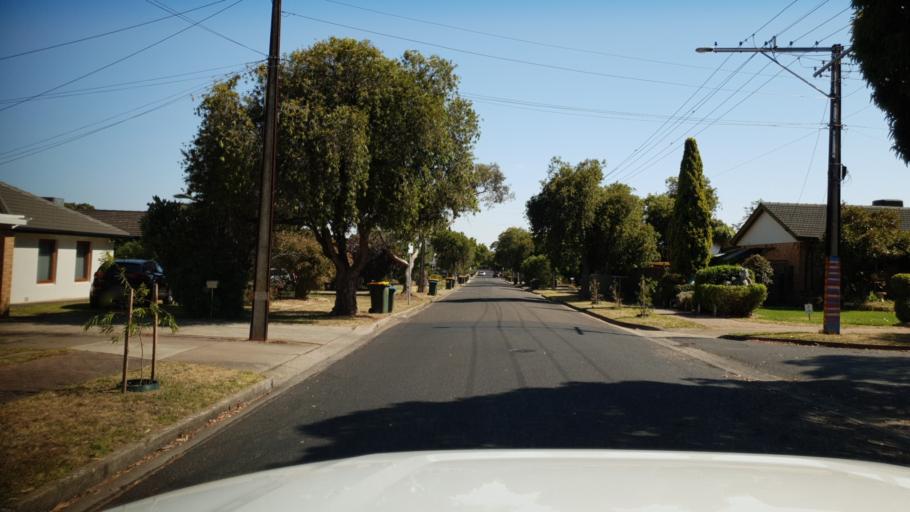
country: AU
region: South Australia
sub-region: Mitcham
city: Clapham
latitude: -34.9956
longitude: 138.5868
